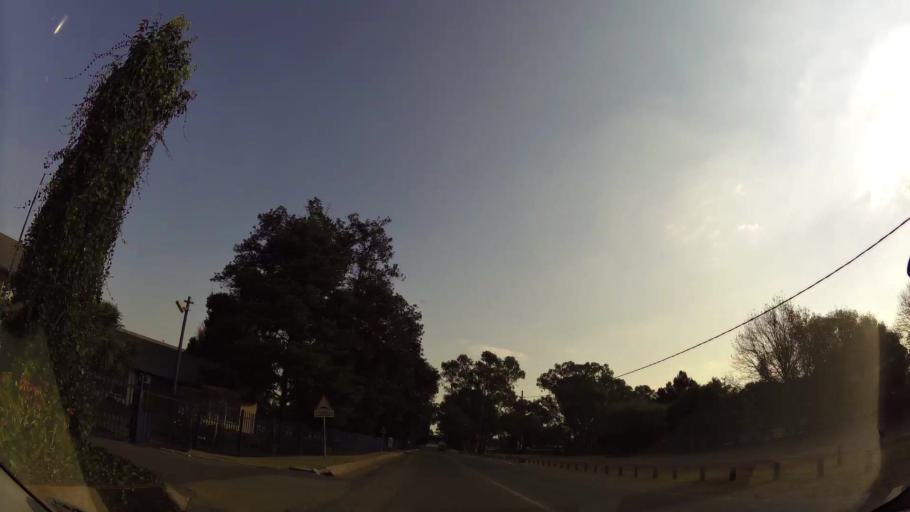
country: ZA
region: Gauteng
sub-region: Ekurhuleni Metropolitan Municipality
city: Benoni
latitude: -26.1082
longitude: 28.3726
